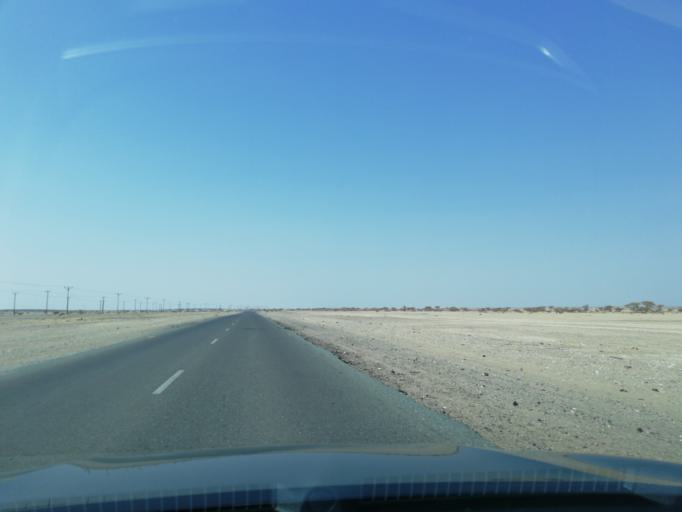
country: OM
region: Muhafazat ad Dakhiliyah
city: Adam
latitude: 22.3341
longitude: 58.0675
